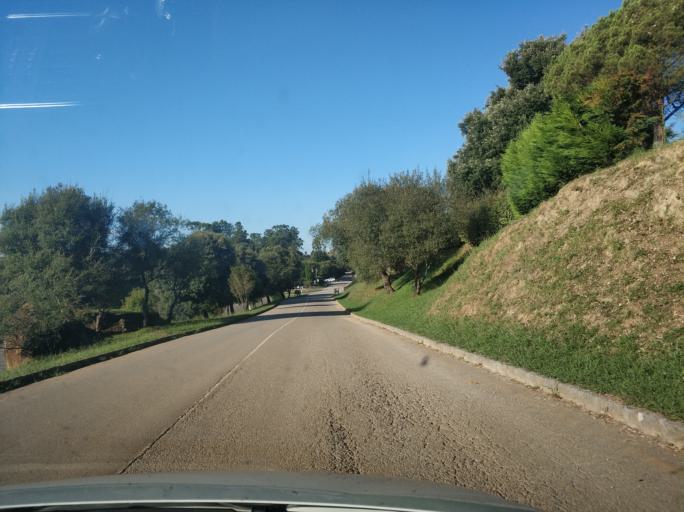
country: ES
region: Cantabria
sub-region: Provincia de Cantabria
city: Penagos
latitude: 43.3576
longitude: -3.8330
